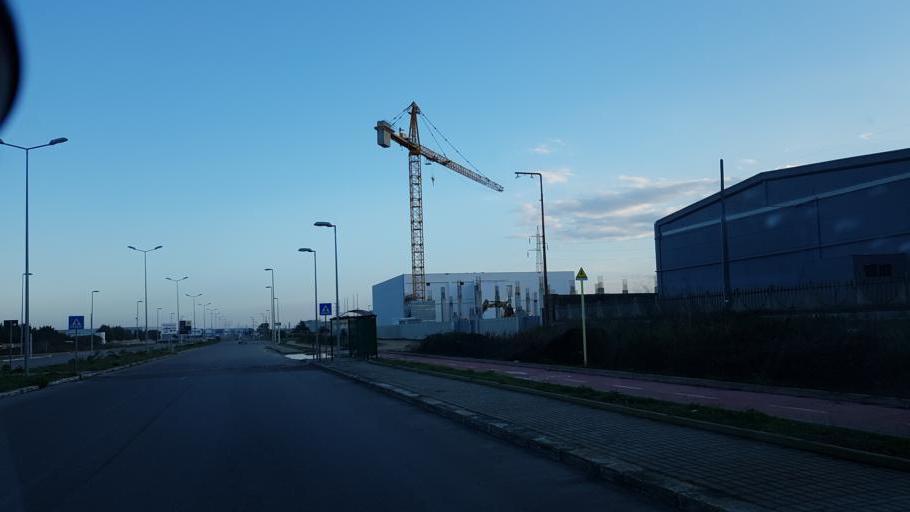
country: IT
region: Apulia
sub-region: Provincia di Lecce
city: Surbo
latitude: 40.3769
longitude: 18.1310
